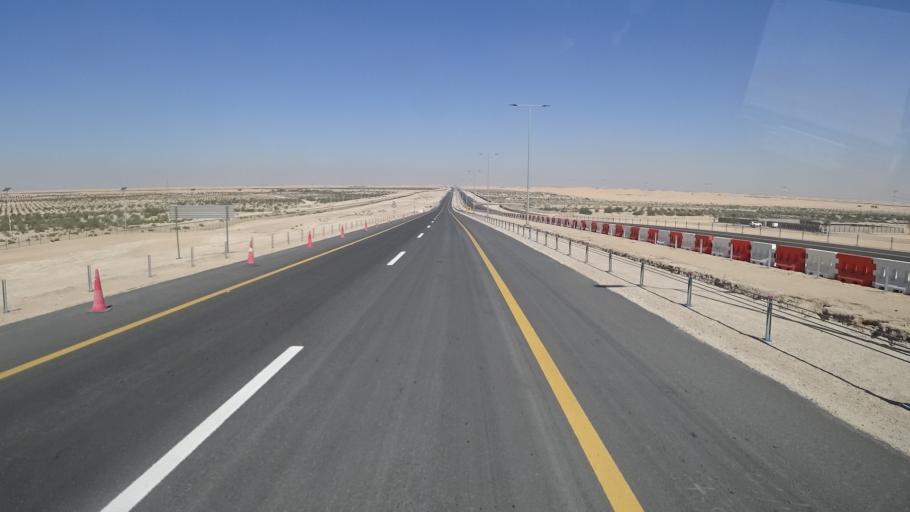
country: AE
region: Abu Dhabi
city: Abu Dhabi
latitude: 24.1350
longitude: 54.8400
